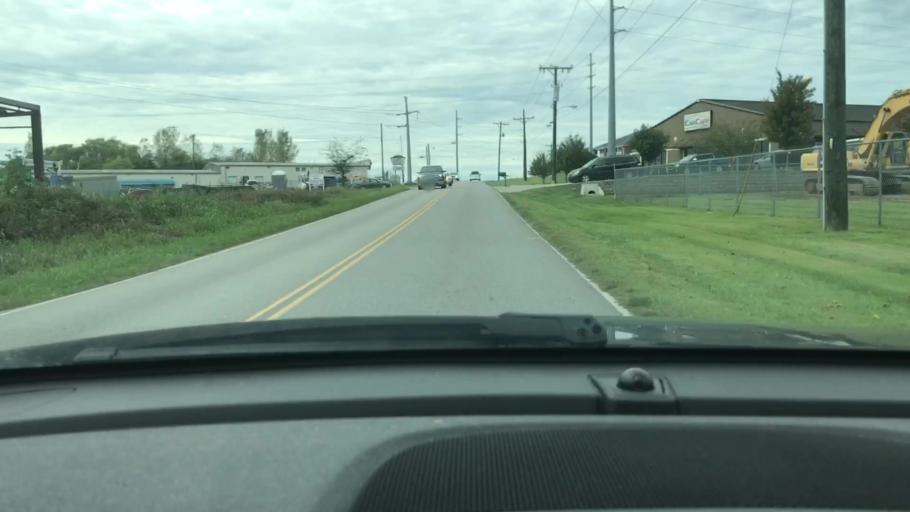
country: US
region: Tennessee
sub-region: Sumner County
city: Hendersonville
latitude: 36.3031
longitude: -86.6515
